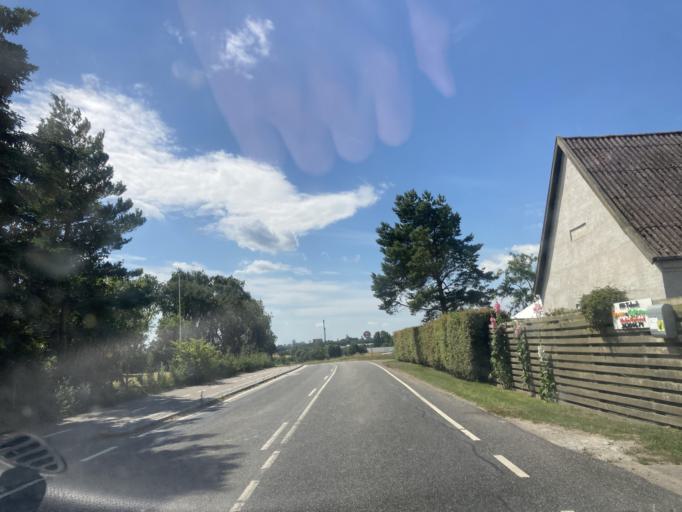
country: DK
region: Zealand
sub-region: Solrod Kommune
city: Solrod
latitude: 55.5187
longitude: 12.1562
